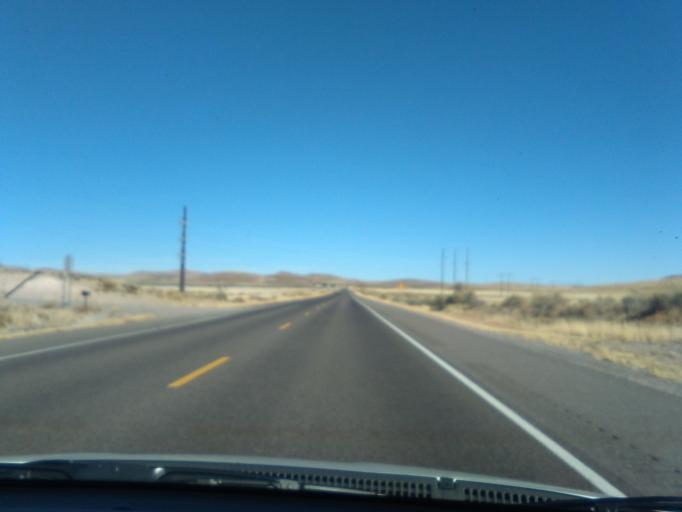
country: US
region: New Mexico
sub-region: Dona Ana County
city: Hatch
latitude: 32.5629
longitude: -107.4672
